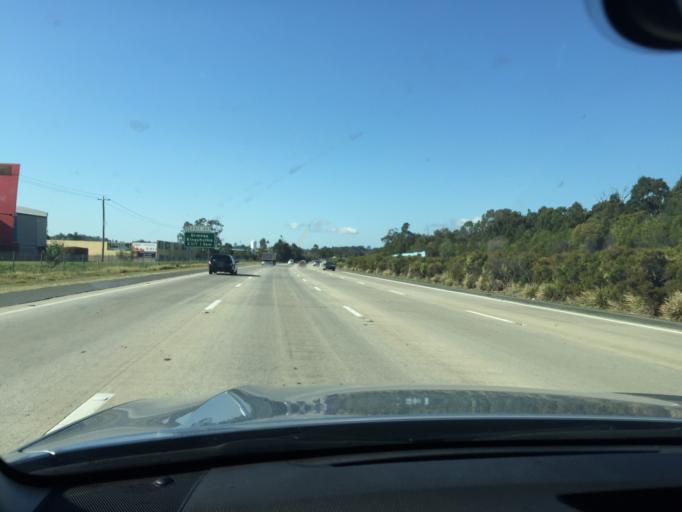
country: AU
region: Queensland
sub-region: Gold Coast
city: Ormeau Hills
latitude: -27.7681
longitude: 153.2505
